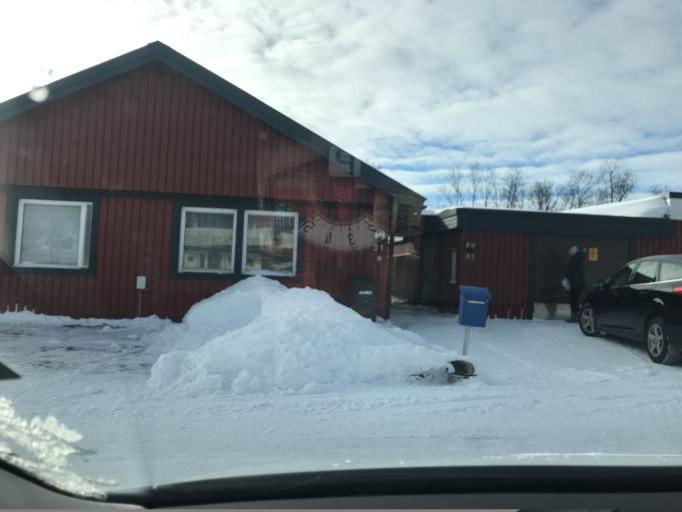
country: SE
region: Norrbotten
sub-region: Kiruna Kommun
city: Kiruna
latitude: 67.8672
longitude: 20.2044
